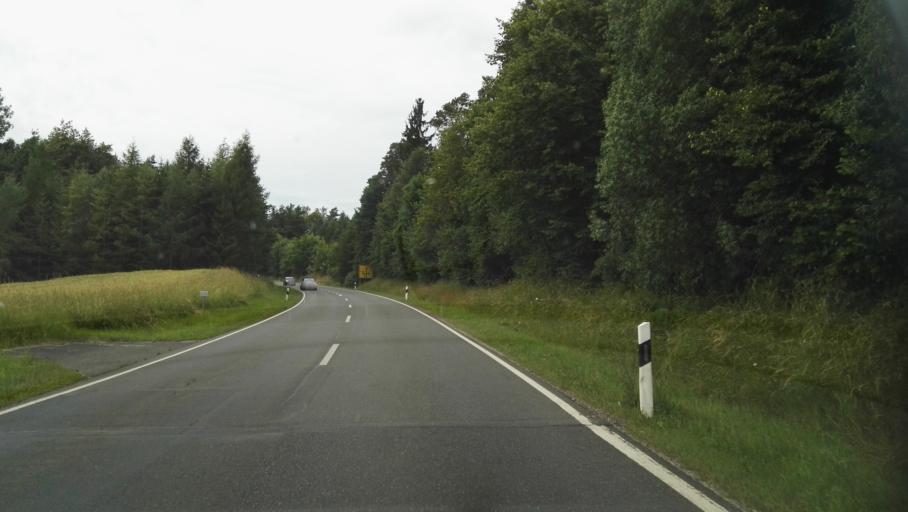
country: DE
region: Bavaria
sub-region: Upper Franconia
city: Plankenfels
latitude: 49.9078
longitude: 11.3246
